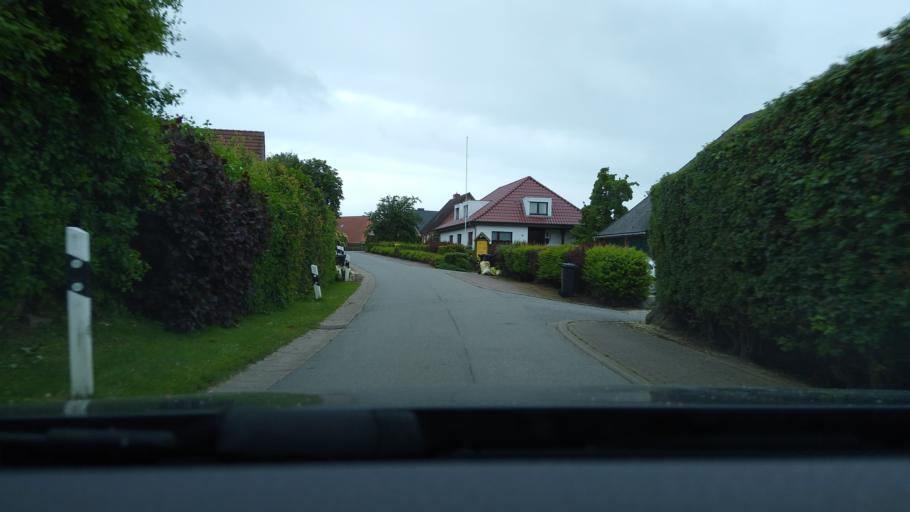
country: DE
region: Schleswig-Holstein
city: Kabelhorst
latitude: 54.2283
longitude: 10.9248
